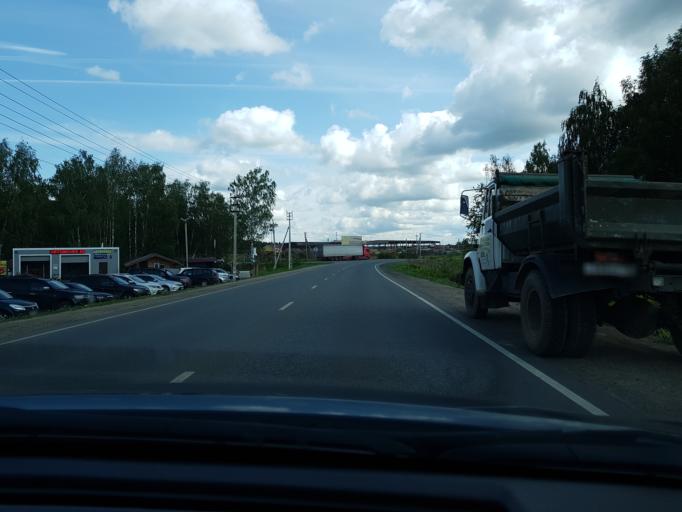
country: RU
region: Moskovskaya
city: Istra
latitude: 55.9717
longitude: 36.9523
